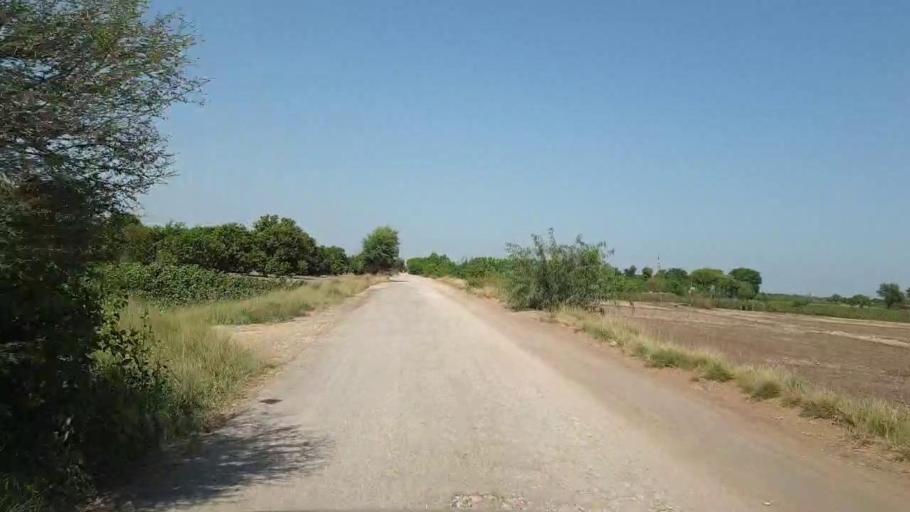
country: PK
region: Sindh
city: Tando Jam
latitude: 25.4829
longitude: 68.4629
